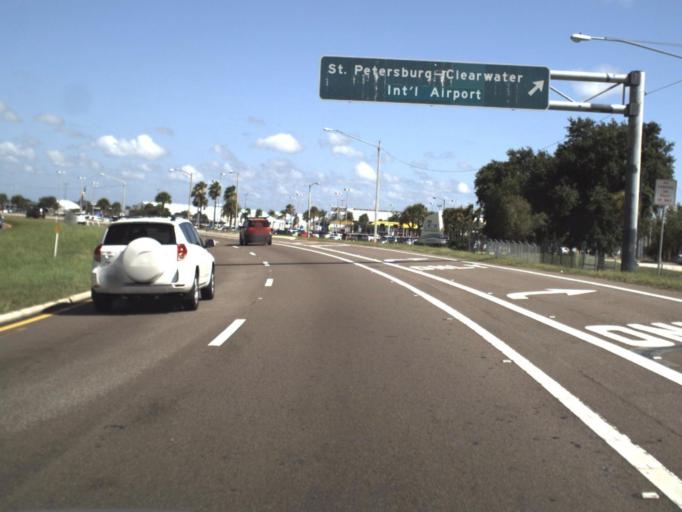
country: US
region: Florida
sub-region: Pinellas County
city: South Highpoint
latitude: 27.9032
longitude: -82.6928
